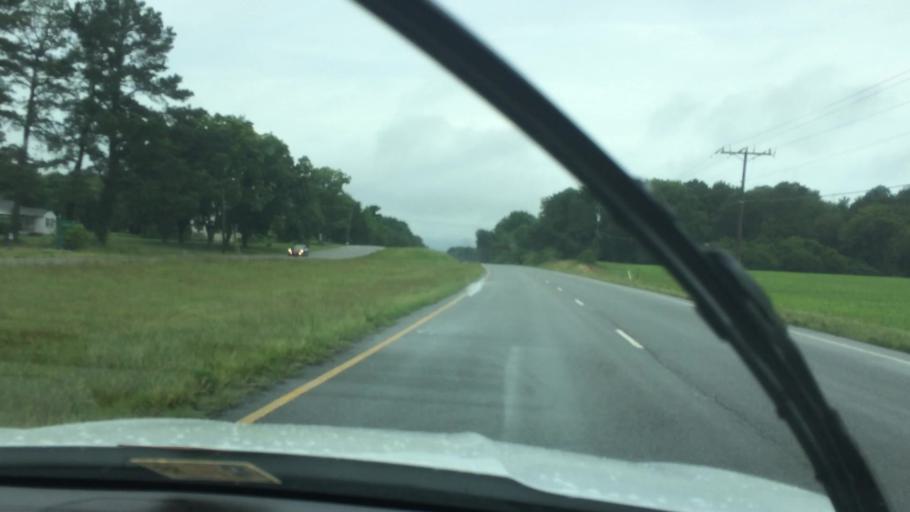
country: US
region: Virginia
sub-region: King William County
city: West Point
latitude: 37.5479
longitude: -76.7372
